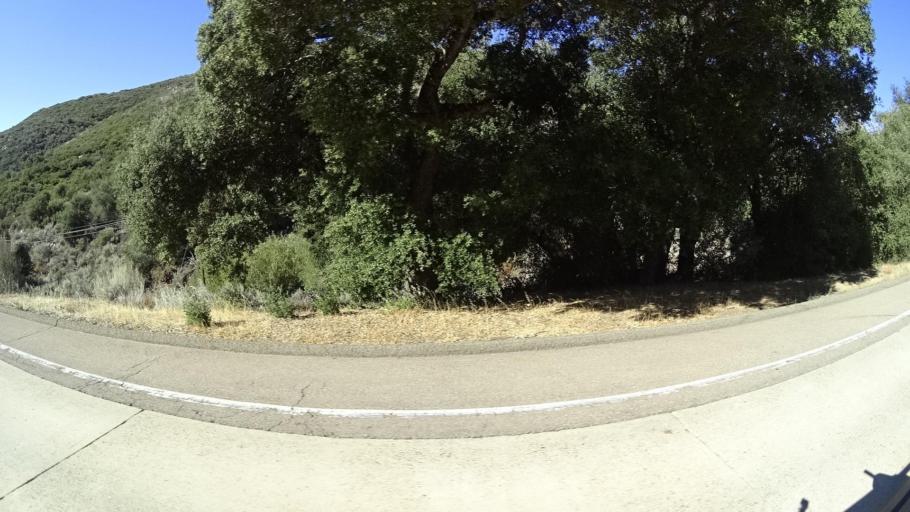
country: US
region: California
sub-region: San Diego County
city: Pine Valley
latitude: 32.8445
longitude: -116.5455
